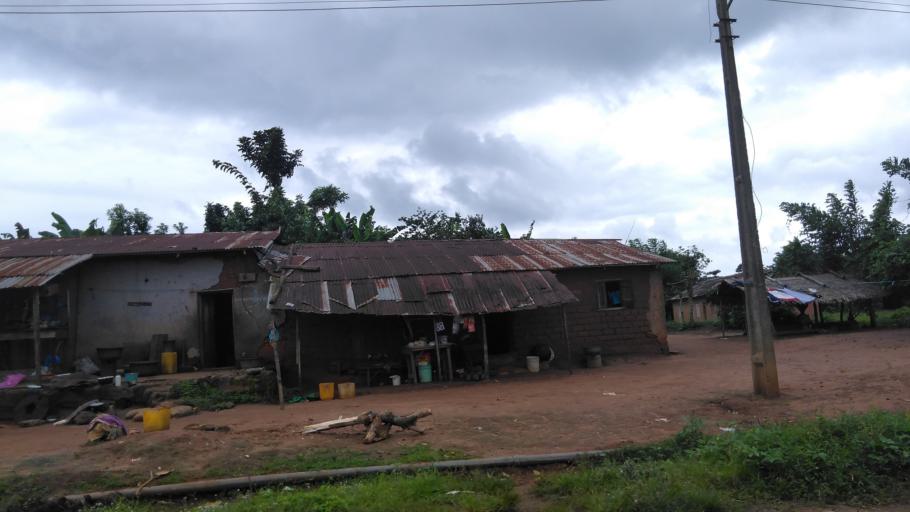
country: NG
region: Ogun
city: Abigi
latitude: 6.5989
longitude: 4.4904
